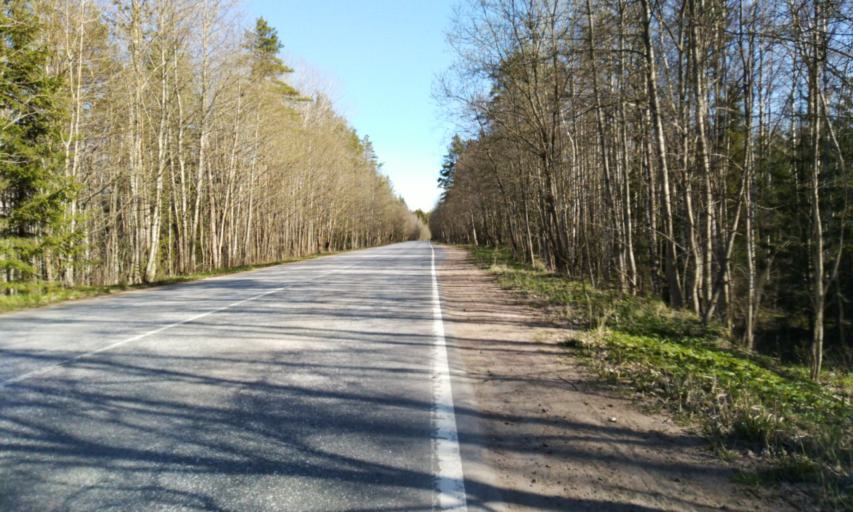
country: RU
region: Leningrad
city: Garbolovo
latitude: 60.3519
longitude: 30.4436
